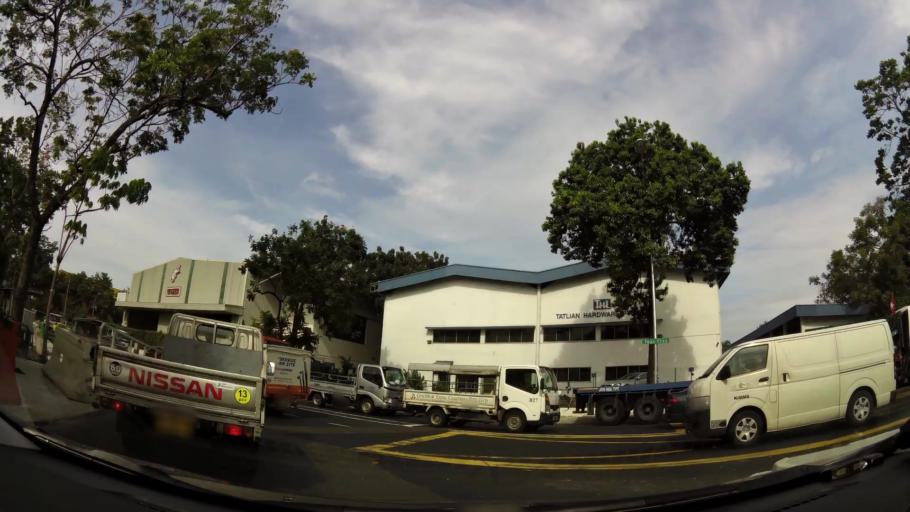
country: MY
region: Johor
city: Johor Bahru
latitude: 1.3194
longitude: 103.6490
